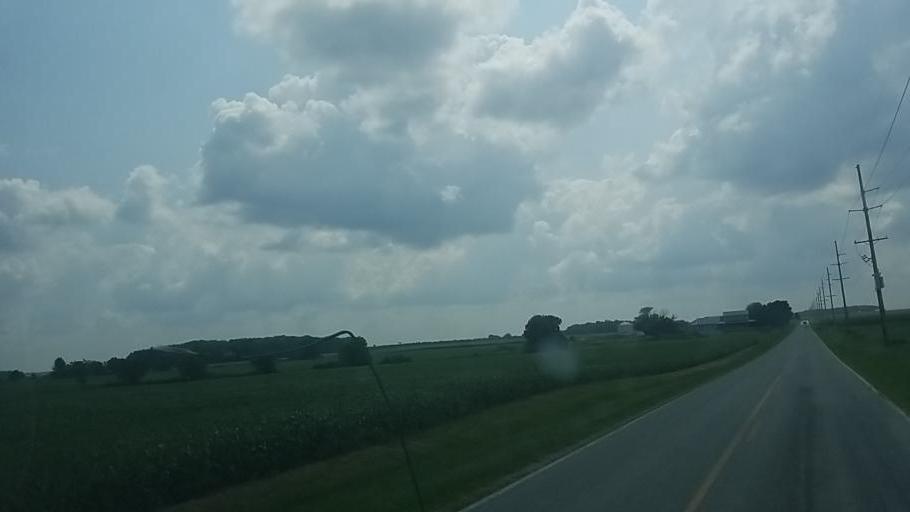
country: US
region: Ohio
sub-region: Wyandot County
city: Upper Sandusky
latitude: 40.8739
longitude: -83.3042
